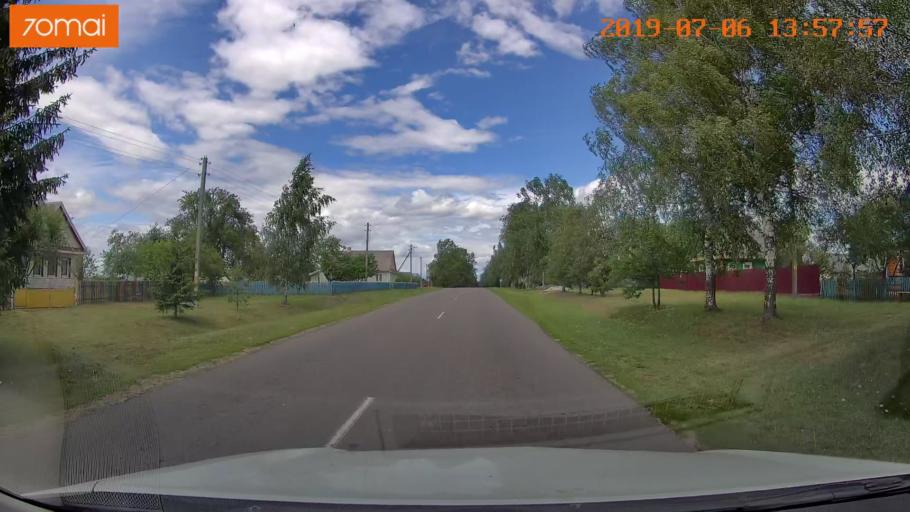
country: BY
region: Minsk
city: Ivyanyets
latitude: 53.7790
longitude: 26.8075
